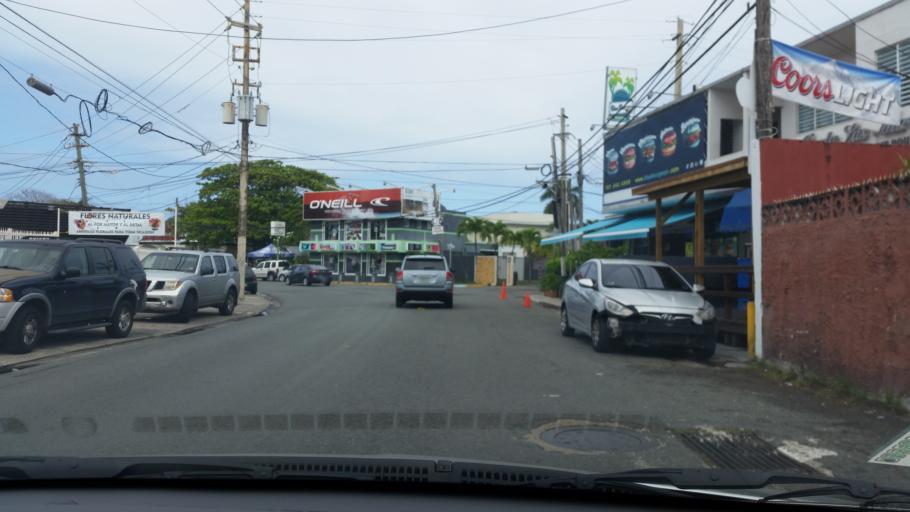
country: PR
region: San Juan
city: San Juan
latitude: 18.4513
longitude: -66.0390
